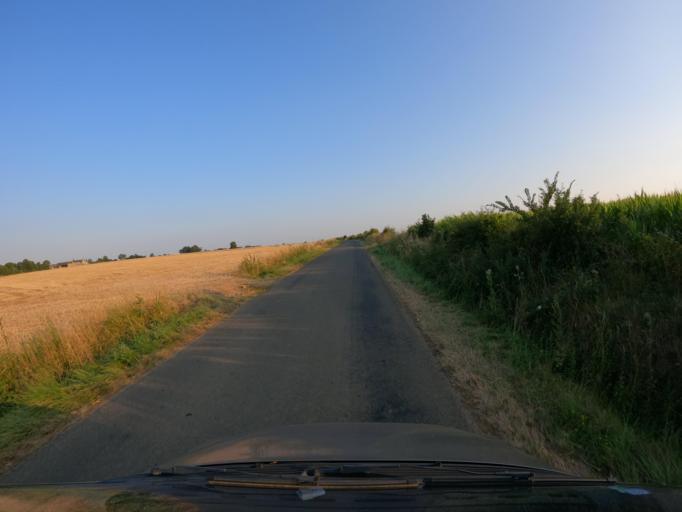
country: FR
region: Pays de la Loire
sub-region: Departement de la Sarthe
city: Brulon
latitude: 47.9233
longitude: -0.2291
